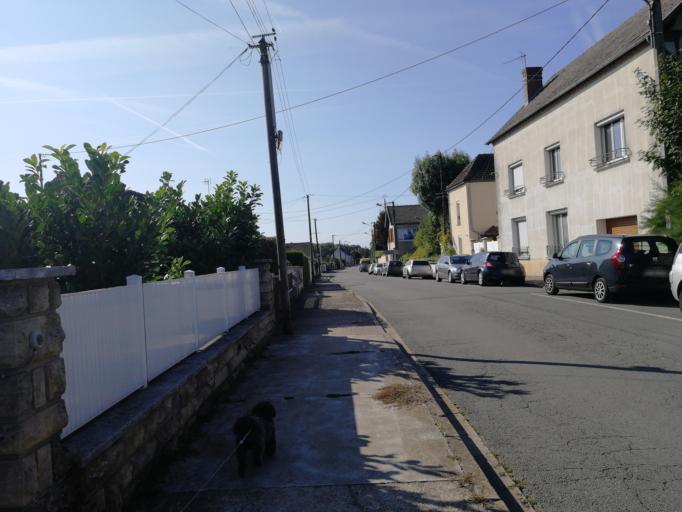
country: FR
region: Centre
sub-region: Departement d'Eure-et-Loir
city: Gallardon
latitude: 48.5260
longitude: 1.6826
